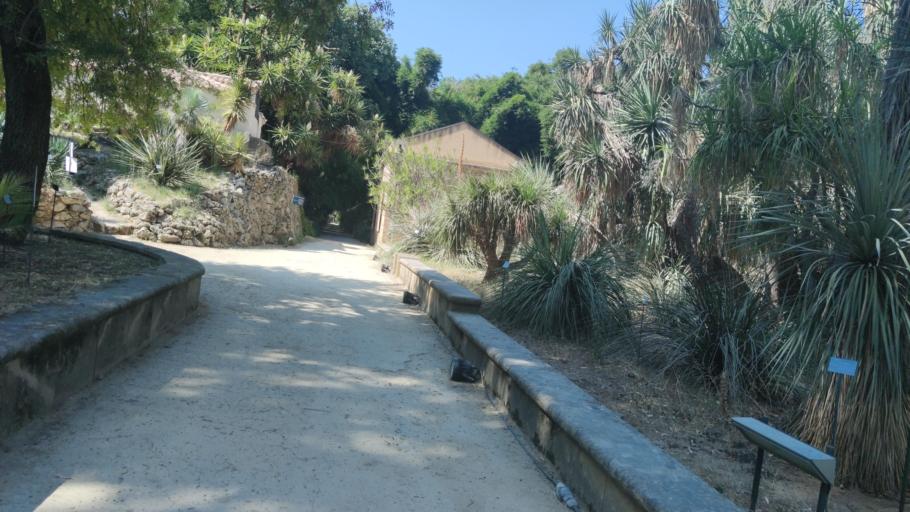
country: IT
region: Sicily
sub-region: Palermo
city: Palermo
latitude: 38.1114
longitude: 13.3743
